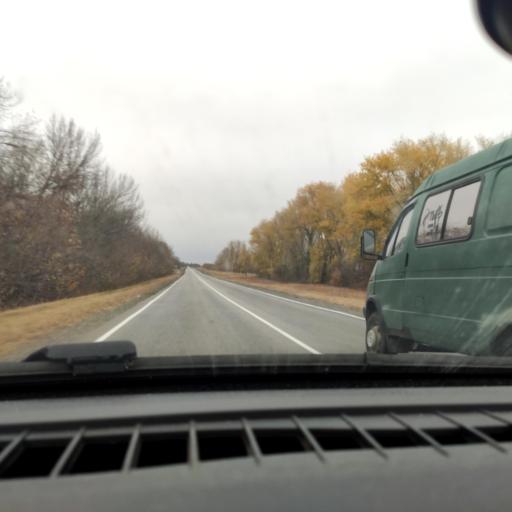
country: RU
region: Voronezj
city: Uryv-Pokrovka
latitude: 51.0884
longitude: 39.0056
